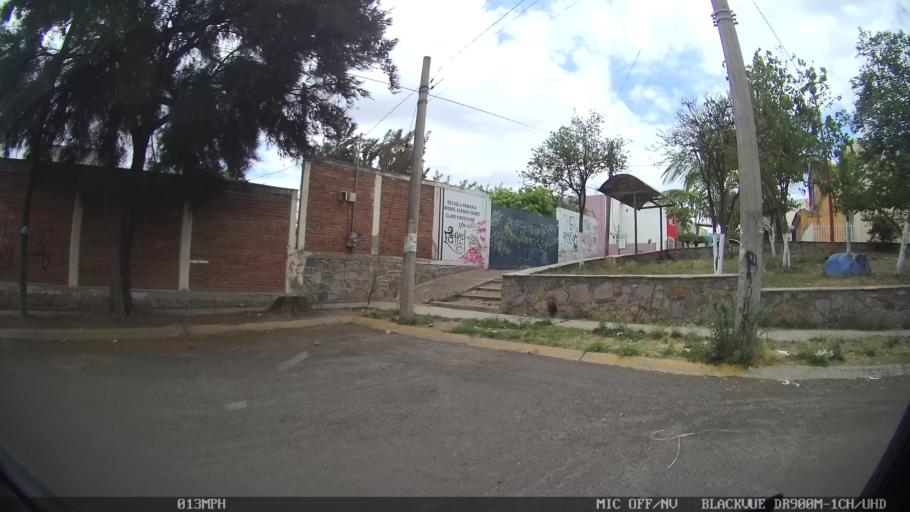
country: MX
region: Jalisco
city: Tonala
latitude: 20.6300
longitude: -103.2589
